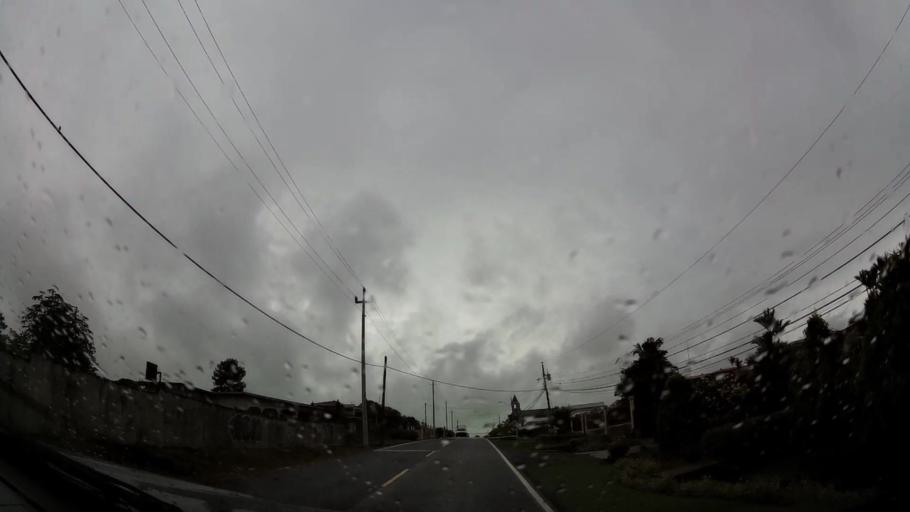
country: PA
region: Veraguas
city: Santiago de Veraguas
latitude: 8.0927
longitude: -80.9588
